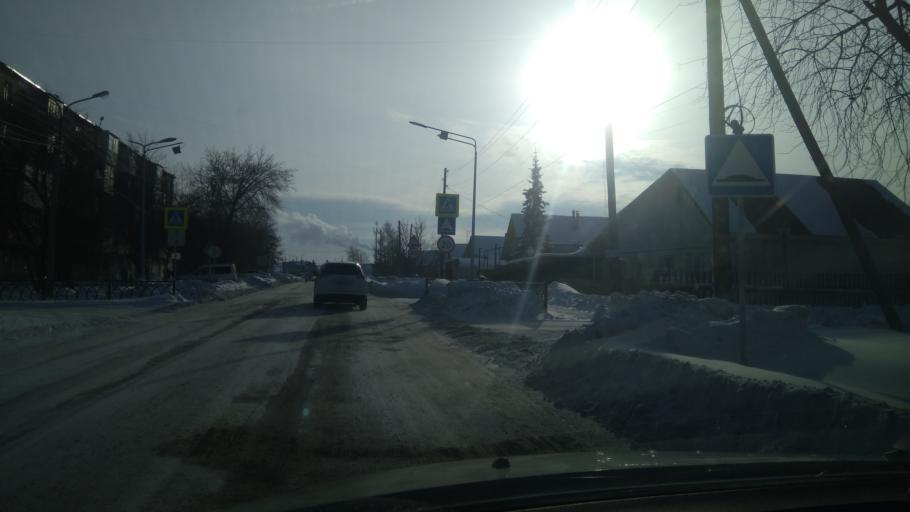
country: RU
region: Sverdlovsk
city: Sukhoy Log
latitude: 56.8946
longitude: 62.0325
